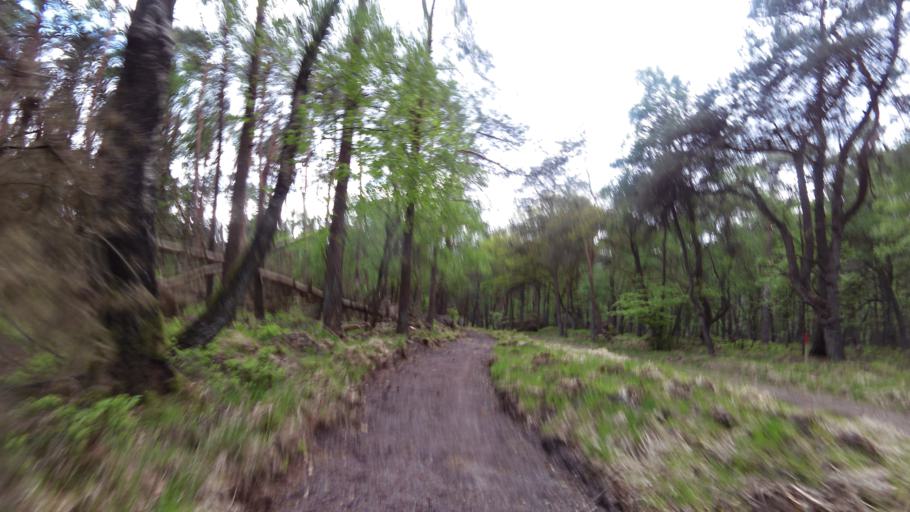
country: NL
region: Gelderland
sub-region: Gemeente Brummen
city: Eerbeek
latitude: 52.0685
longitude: 6.0270
